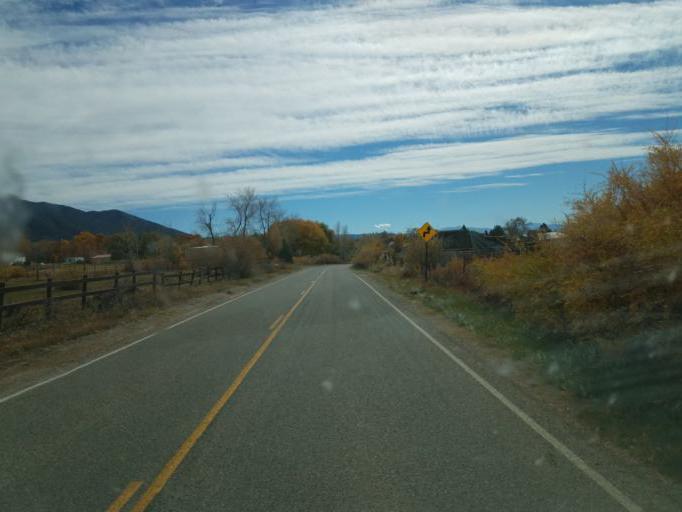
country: US
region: New Mexico
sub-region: Taos County
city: Arroyo Seco
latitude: 36.5201
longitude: -105.5692
